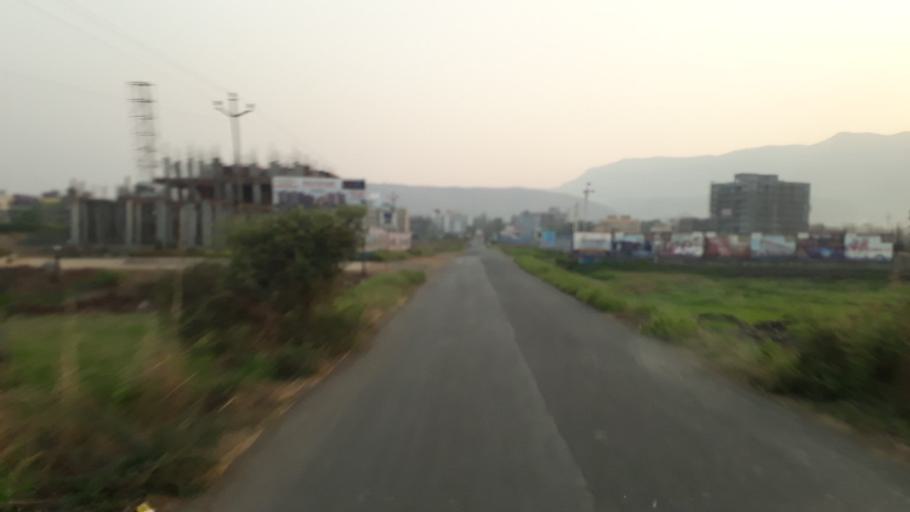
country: IN
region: Maharashtra
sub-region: Raigarh
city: Neral
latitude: 19.0345
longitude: 73.3267
